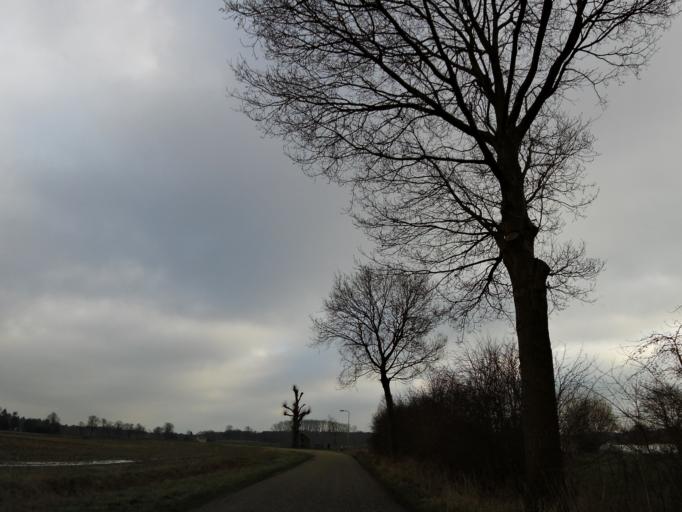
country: NL
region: Limburg
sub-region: Gemeente Bergen
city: Wellerlooi
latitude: 51.5495
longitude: 6.1034
